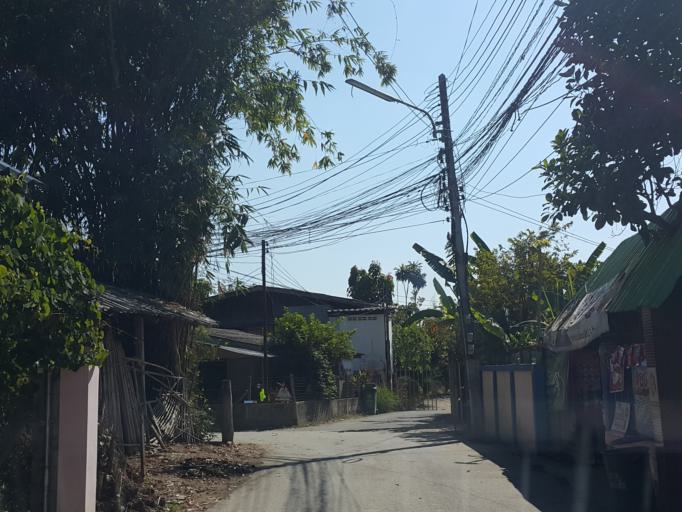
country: TH
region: Chiang Mai
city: San Sai
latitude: 18.8540
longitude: 98.9968
